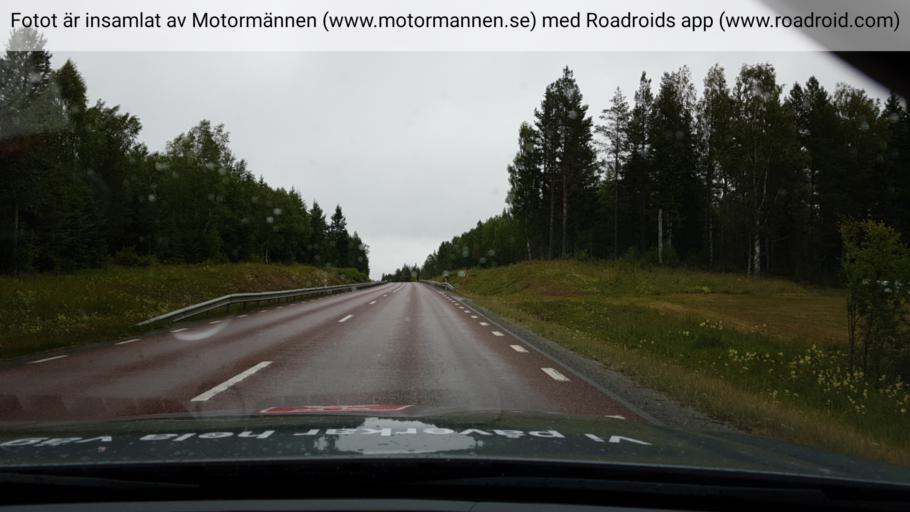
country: SE
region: Jaemtland
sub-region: OEstersunds Kommun
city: Brunflo
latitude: 63.0044
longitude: 14.6763
